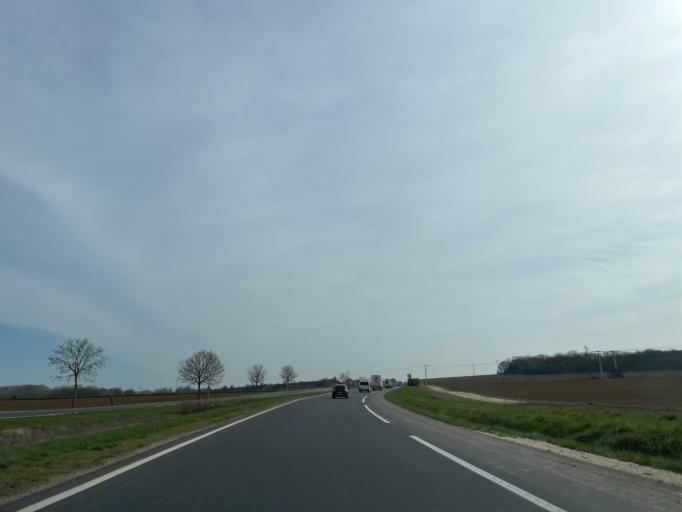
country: FR
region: Champagne-Ardenne
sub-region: Departement de l'Aube
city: Nogent-sur-Seine
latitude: 48.5068
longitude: 3.5645
